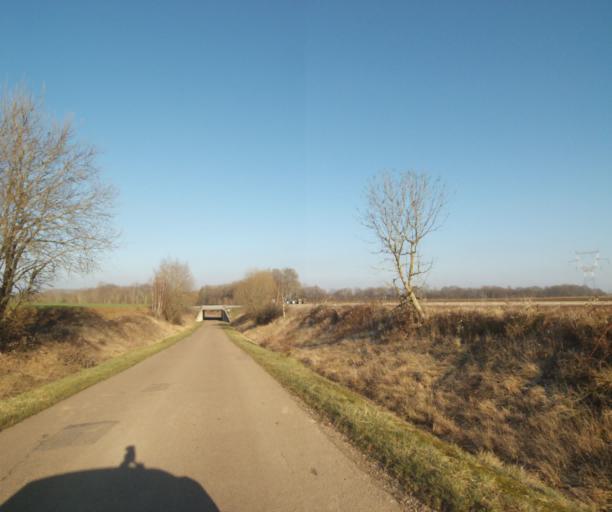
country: FR
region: Champagne-Ardenne
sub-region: Departement de la Haute-Marne
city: Chevillon
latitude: 48.5155
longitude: 5.0903
